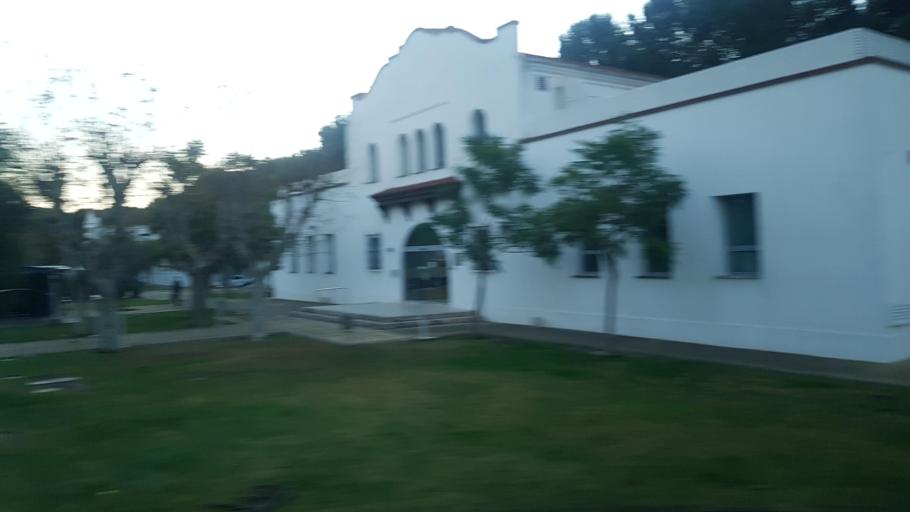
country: ES
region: Valencia
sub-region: Provincia de Valencia
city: Manises
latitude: 39.4785
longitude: -0.4835
